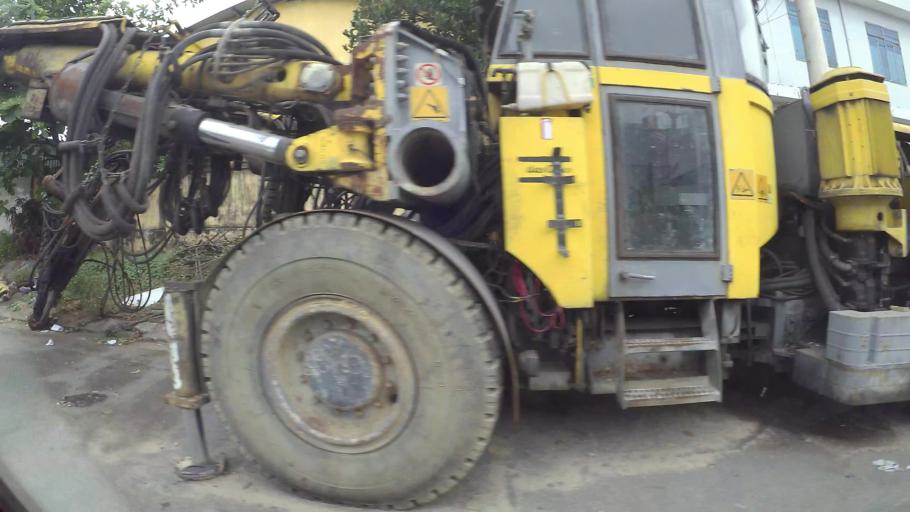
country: VN
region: Da Nang
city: Cam Le
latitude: 16.0357
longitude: 108.2211
